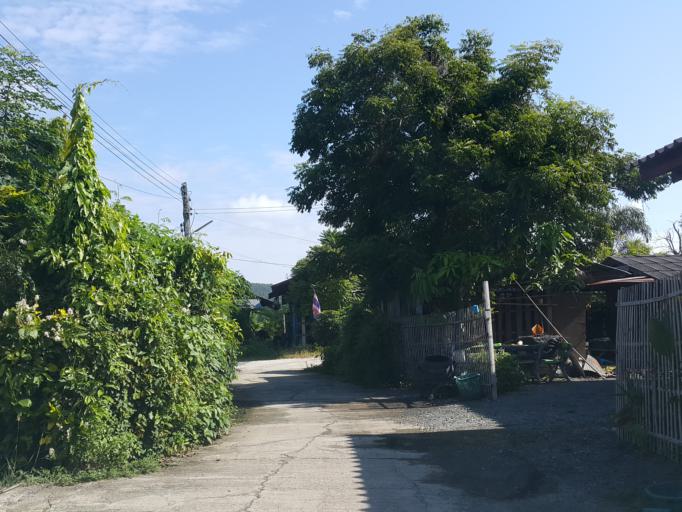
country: TH
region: Chiang Mai
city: Mae On
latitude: 18.8238
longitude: 99.1694
